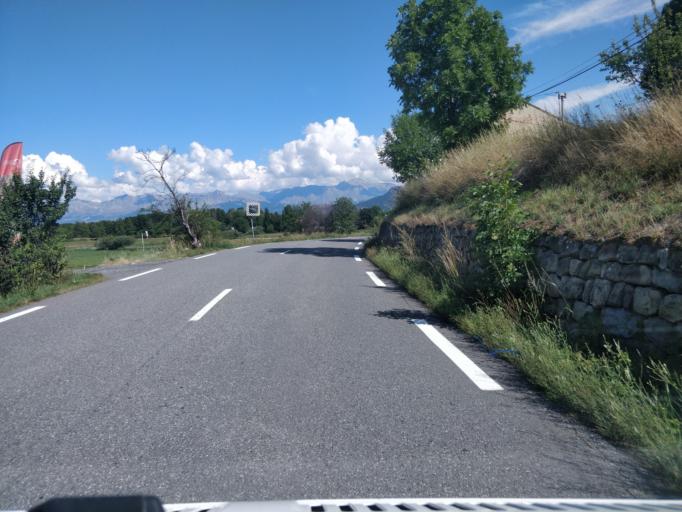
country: FR
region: Provence-Alpes-Cote d'Azur
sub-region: Departement des Alpes-de-Haute-Provence
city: Seyne-les-Alpes
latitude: 44.4169
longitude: 6.3519
